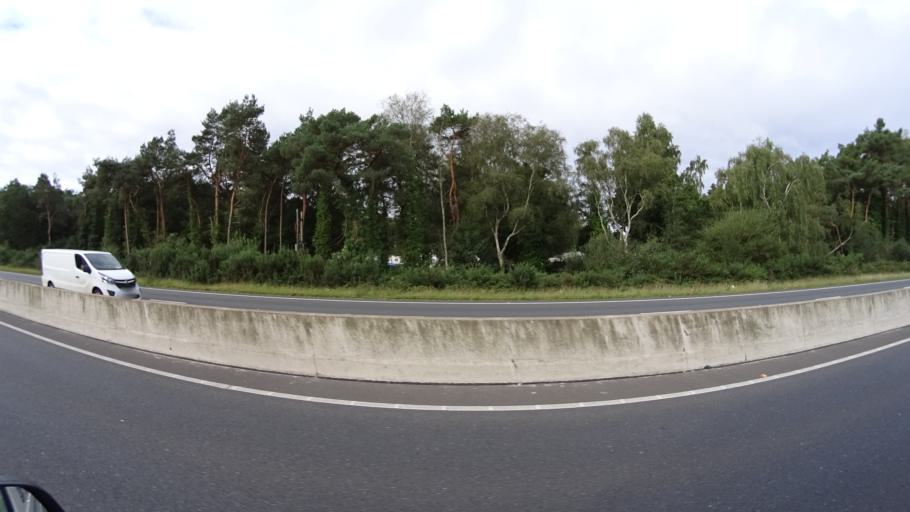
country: GB
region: England
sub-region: Dorset
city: St Leonards
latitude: 50.7864
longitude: -1.8136
